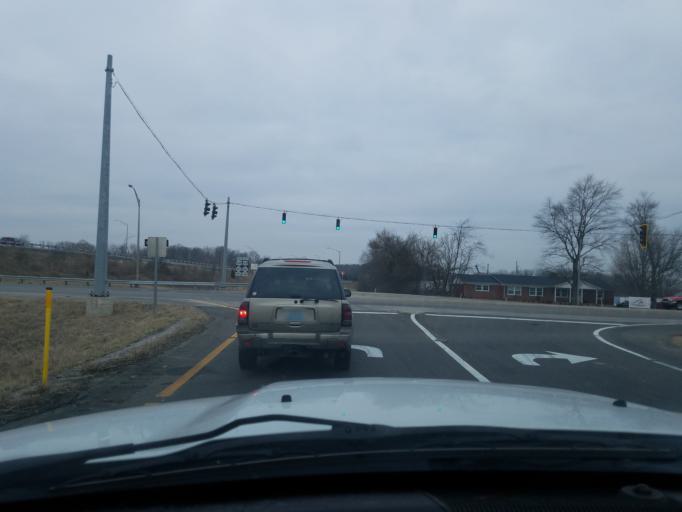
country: US
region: Kentucky
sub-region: Warren County
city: Bowling Green
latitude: 36.9576
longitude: -86.4959
